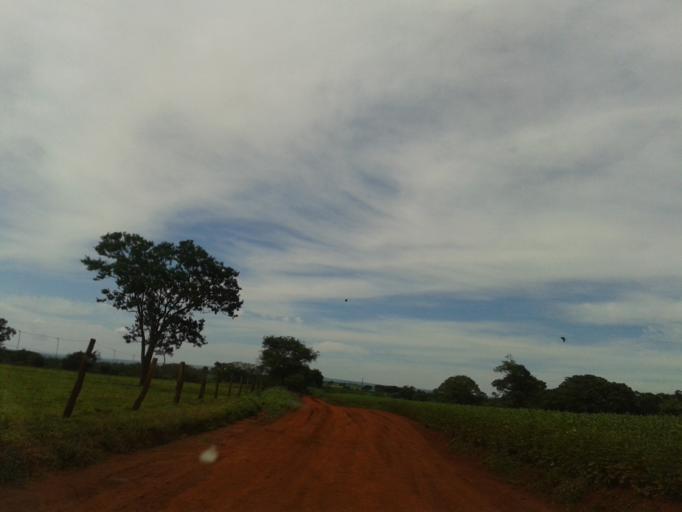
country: BR
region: Minas Gerais
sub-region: Capinopolis
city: Capinopolis
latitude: -18.7350
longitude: -49.8445
